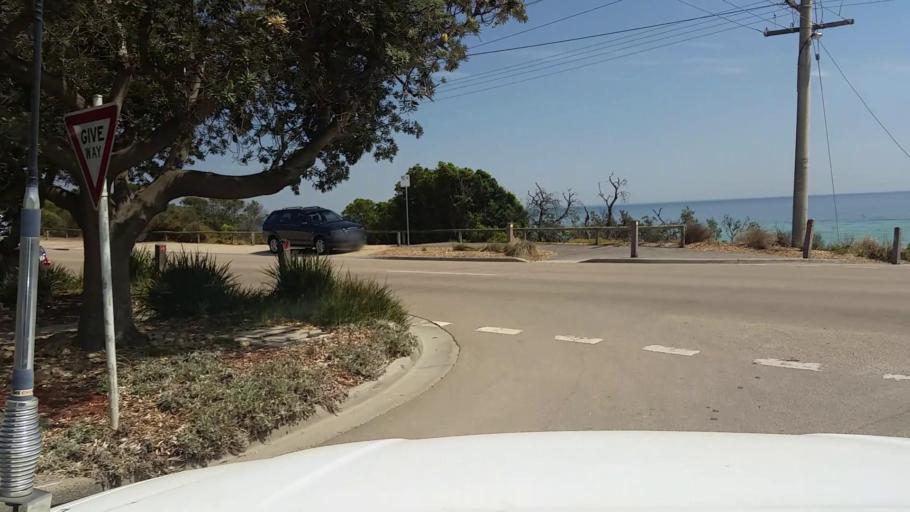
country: AU
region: Victoria
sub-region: Mornington Peninsula
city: Mount Martha
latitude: -38.2698
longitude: 145.0098
